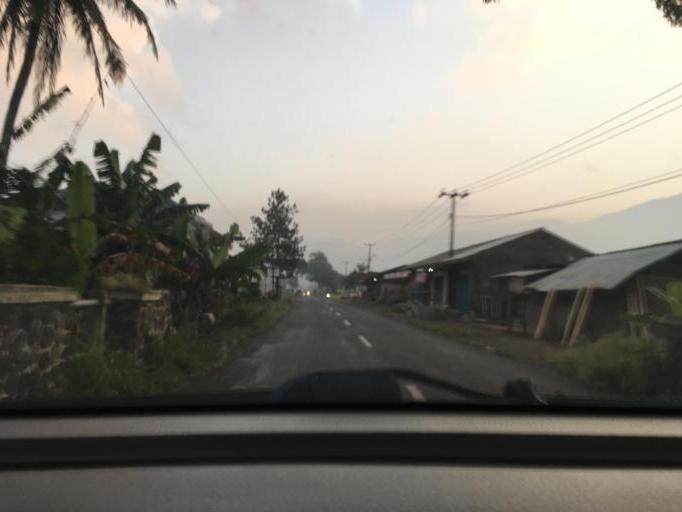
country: ID
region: West Java
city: Padamulya
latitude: -7.2022
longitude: 108.1995
